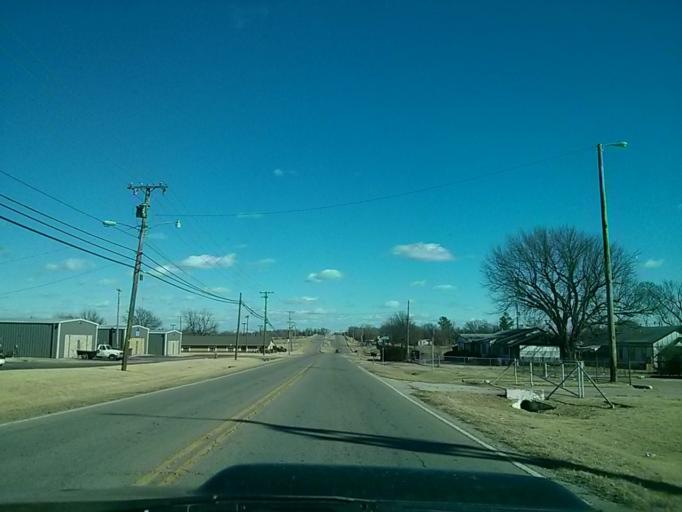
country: US
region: Oklahoma
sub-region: Tulsa County
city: Turley
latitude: 36.2061
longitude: -95.9534
